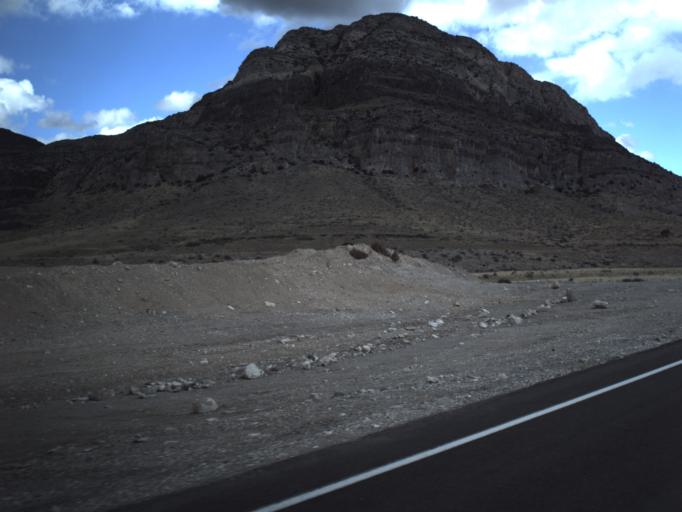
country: US
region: Utah
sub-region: Beaver County
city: Milford
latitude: 38.5058
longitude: -113.6063
